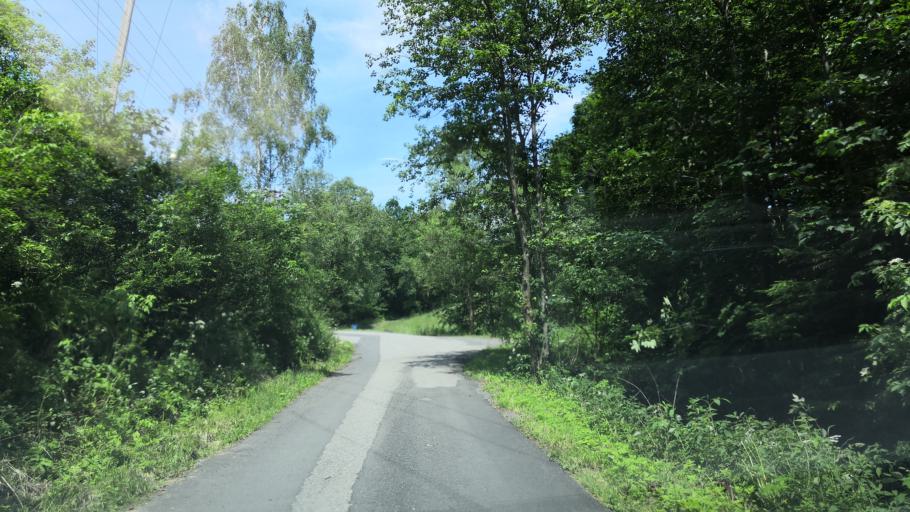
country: CZ
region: Zlin
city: Valasska Bystrice
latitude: 49.4214
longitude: 18.0980
